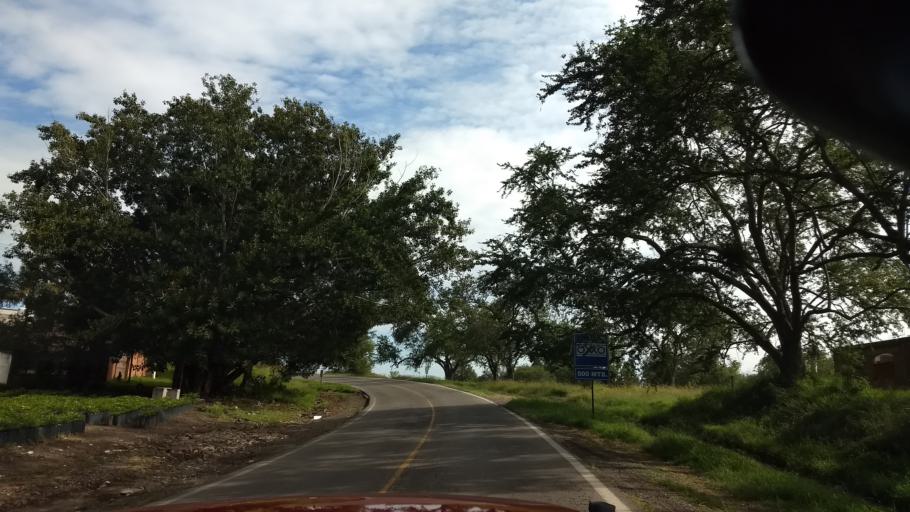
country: MX
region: Jalisco
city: Tuxpan
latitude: 19.5512
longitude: -103.3912
